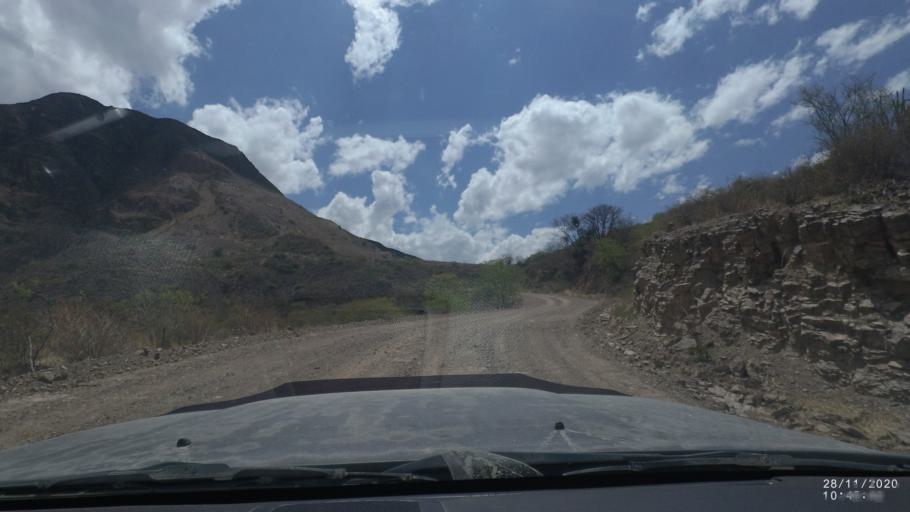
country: BO
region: Cochabamba
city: Capinota
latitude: -17.7867
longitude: -66.1293
